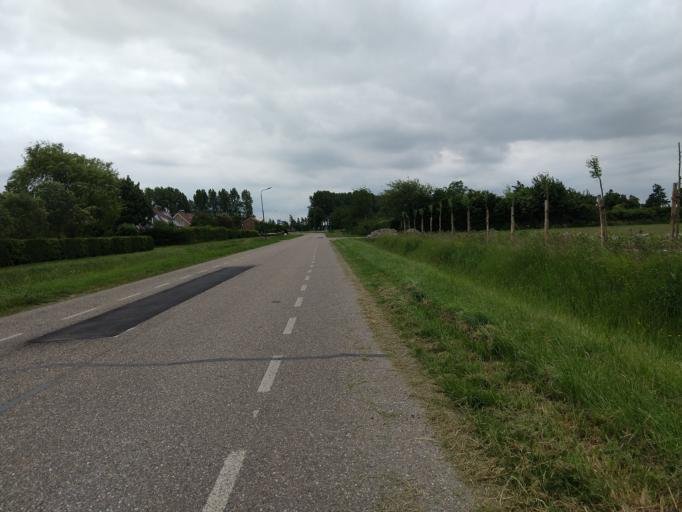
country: NL
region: Zeeland
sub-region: Gemeente Borsele
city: Borssele
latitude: 51.4668
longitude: 3.8068
